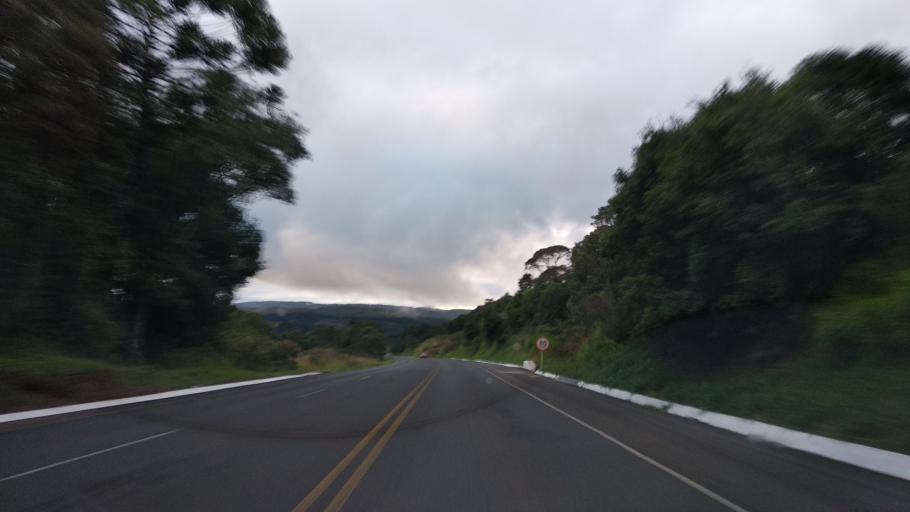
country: BR
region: Santa Catarina
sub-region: Campos Novos
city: Campos Novos
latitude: -27.4405
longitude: -51.0117
